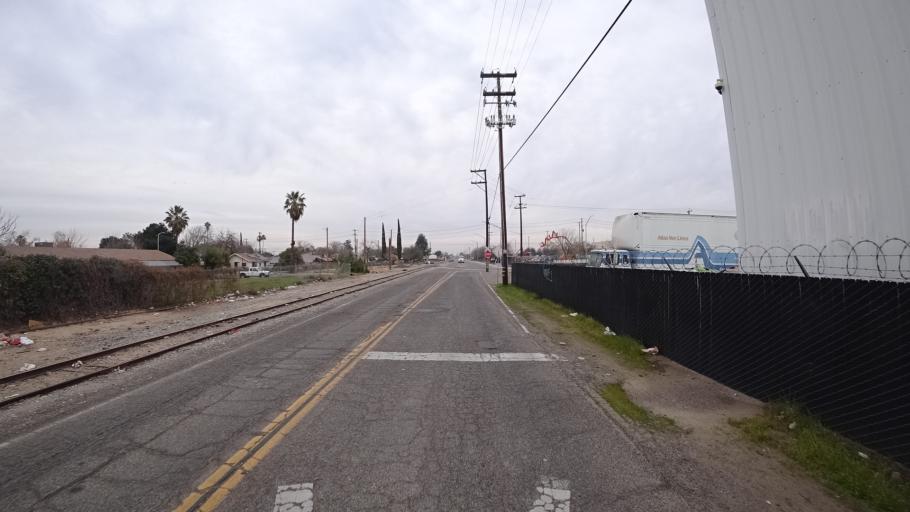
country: US
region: California
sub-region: Fresno County
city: Fresno
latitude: 36.7213
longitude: -119.7677
